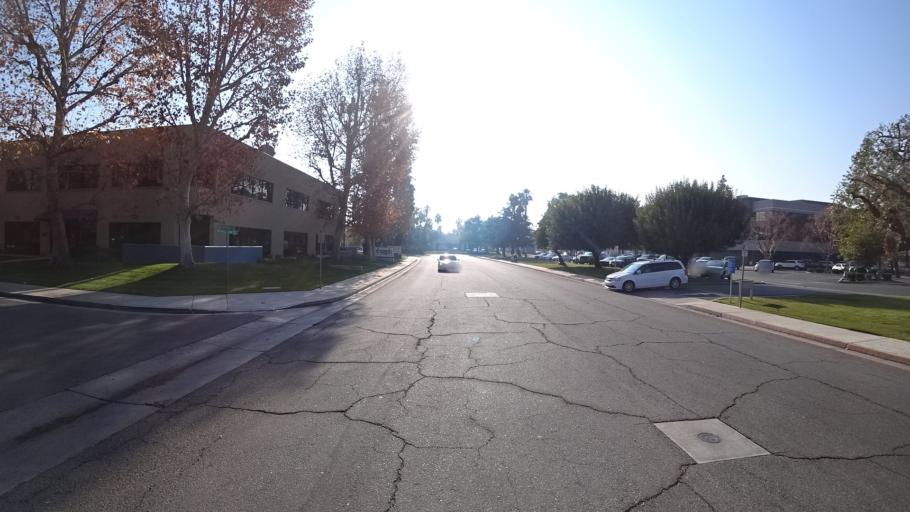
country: US
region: California
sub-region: Kern County
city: Bakersfield
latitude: 35.3614
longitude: -119.0582
